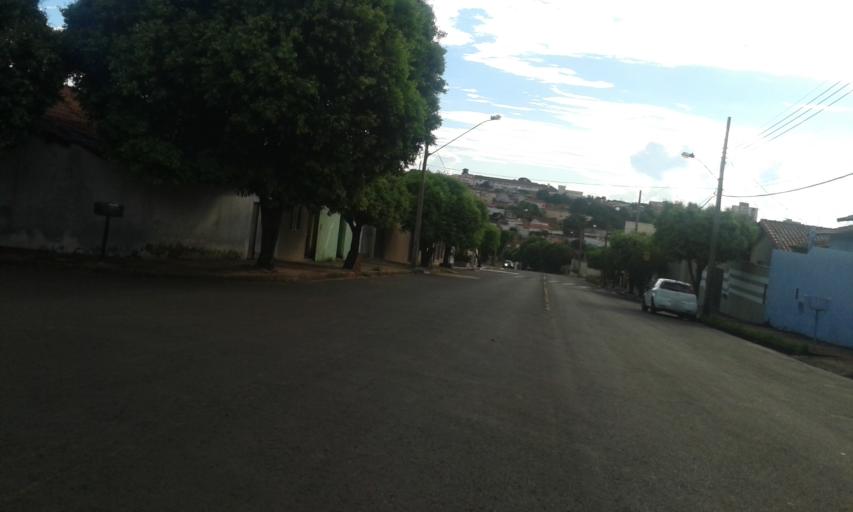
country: BR
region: Minas Gerais
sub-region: Ituiutaba
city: Ituiutaba
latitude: -18.9630
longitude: -49.4587
